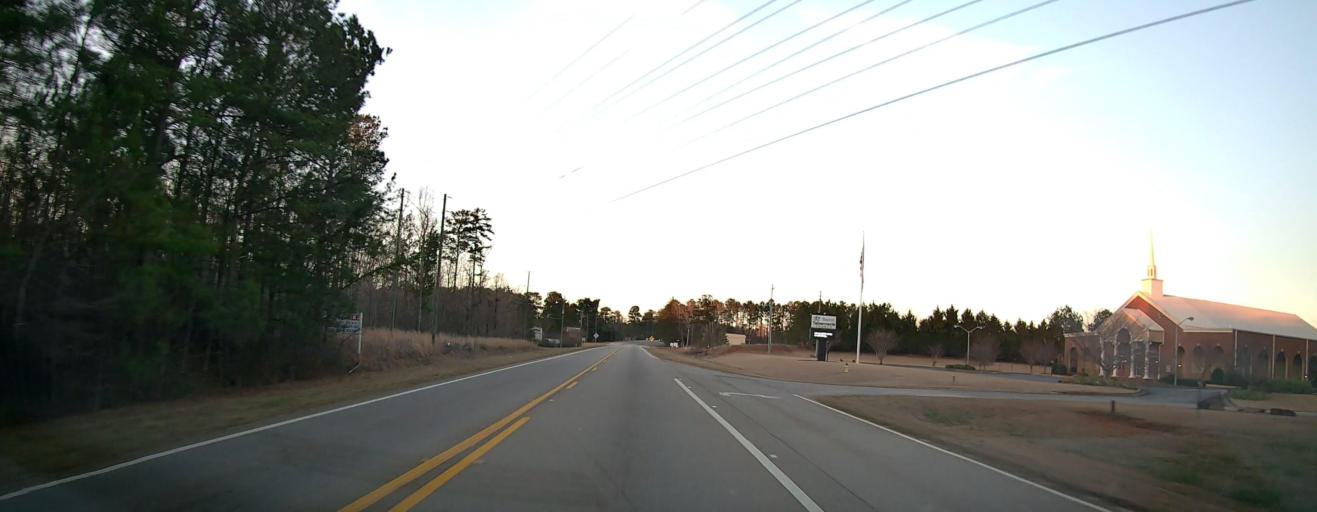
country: US
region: Georgia
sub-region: Troup County
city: La Grange
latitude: 33.0313
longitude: -84.9881
